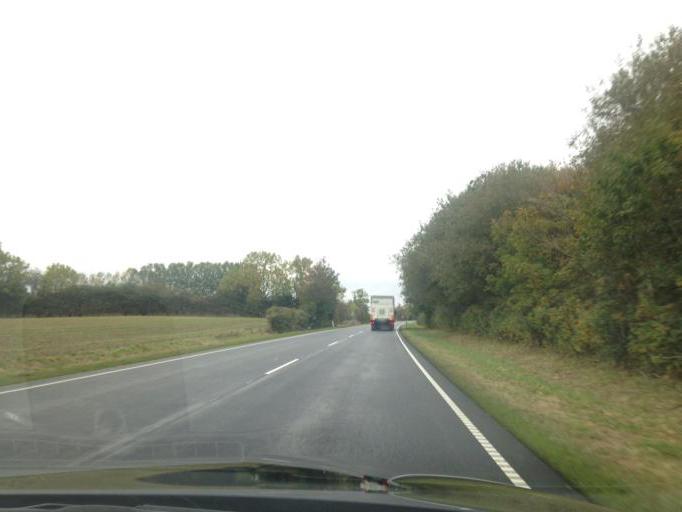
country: DK
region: South Denmark
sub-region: Kolding Kommune
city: Christiansfeld
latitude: 55.3591
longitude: 9.4783
